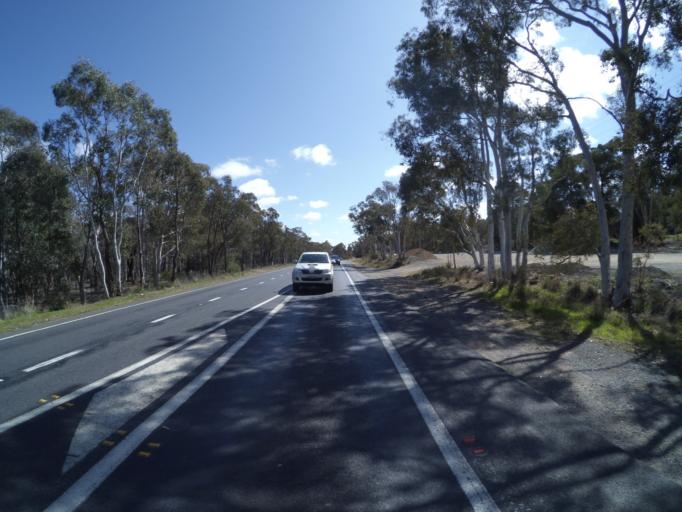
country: AU
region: New South Wales
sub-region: Queanbeyan
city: Queanbeyan
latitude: -35.2572
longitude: 149.2626
